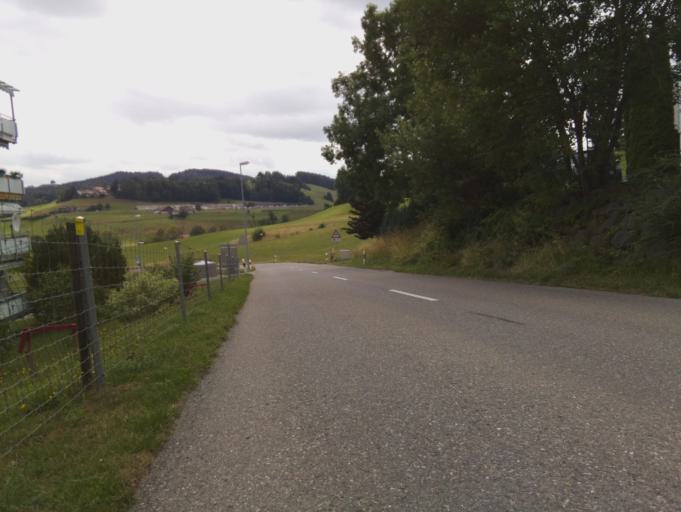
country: CH
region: Saint Gallen
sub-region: Wahlkreis Wil
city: Jonschwil
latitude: 47.4119
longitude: 9.0716
